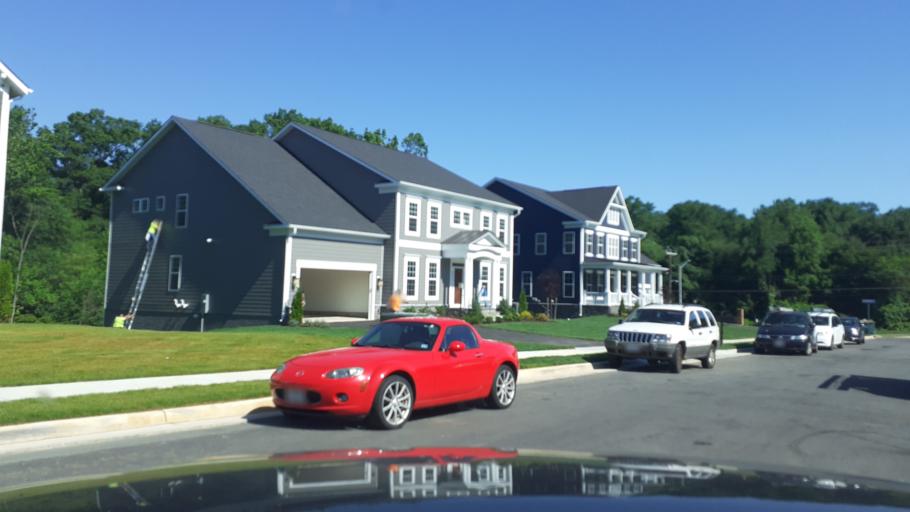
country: US
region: Virginia
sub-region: Fairfax County
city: Mantua
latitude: 38.8641
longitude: -77.2540
